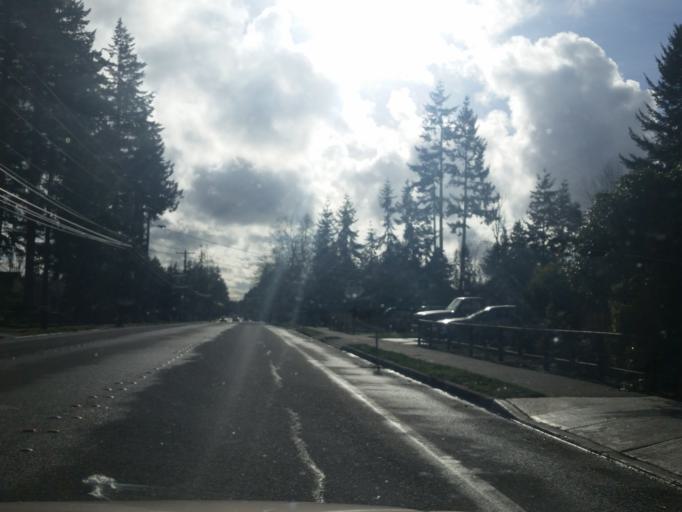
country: US
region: Washington
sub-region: Snohomish County
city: Lynnwood
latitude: 47.8232
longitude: -122.3251
